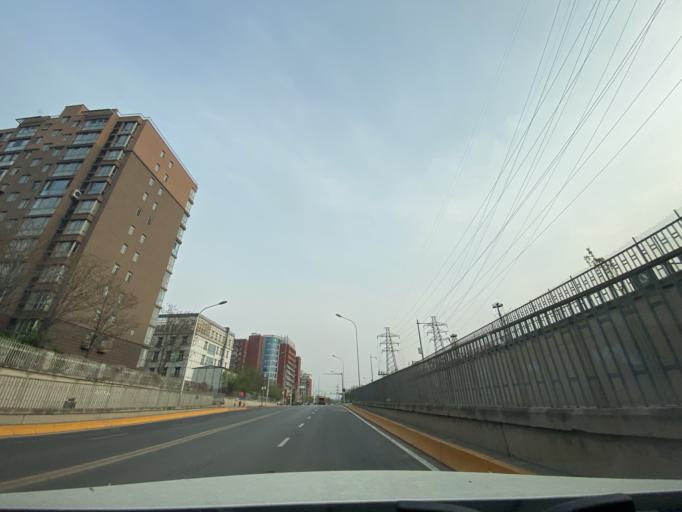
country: CN
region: Beijing
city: Babaoshan
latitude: 39.9296
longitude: 116.2328
